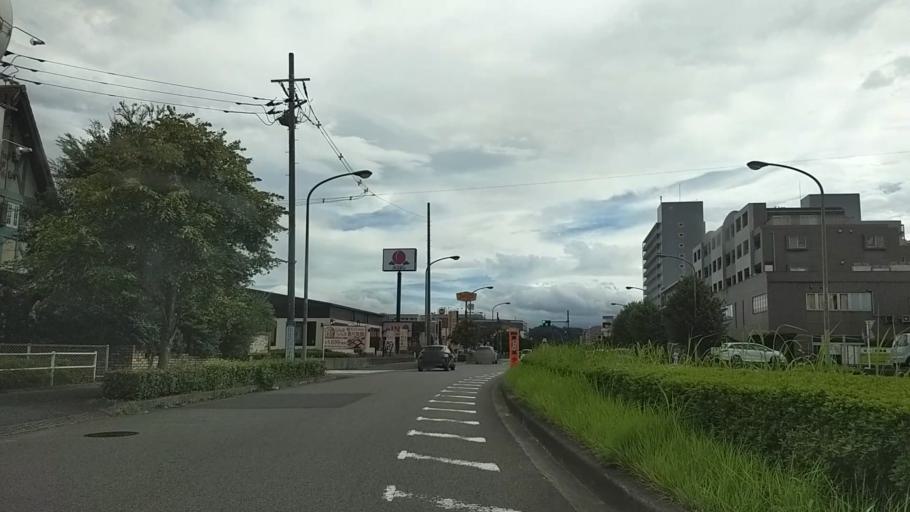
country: JP
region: Tokyo
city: Hachioji
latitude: 35.6350
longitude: 139.3304
